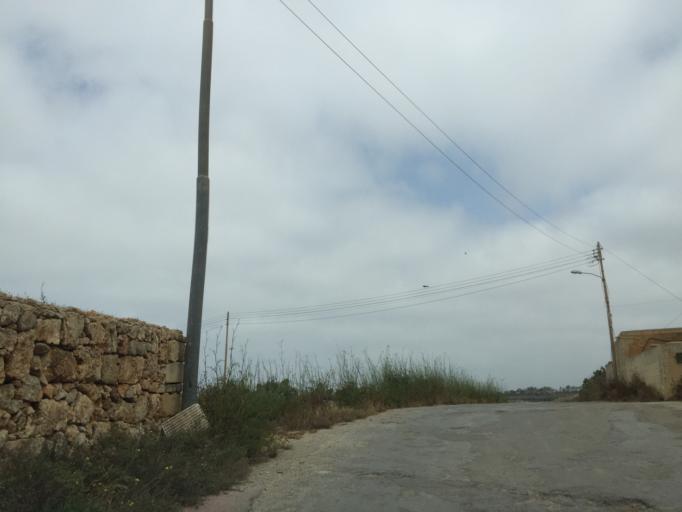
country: MT
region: Dingli
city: Dingli
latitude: 35.8805
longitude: 14.3591
